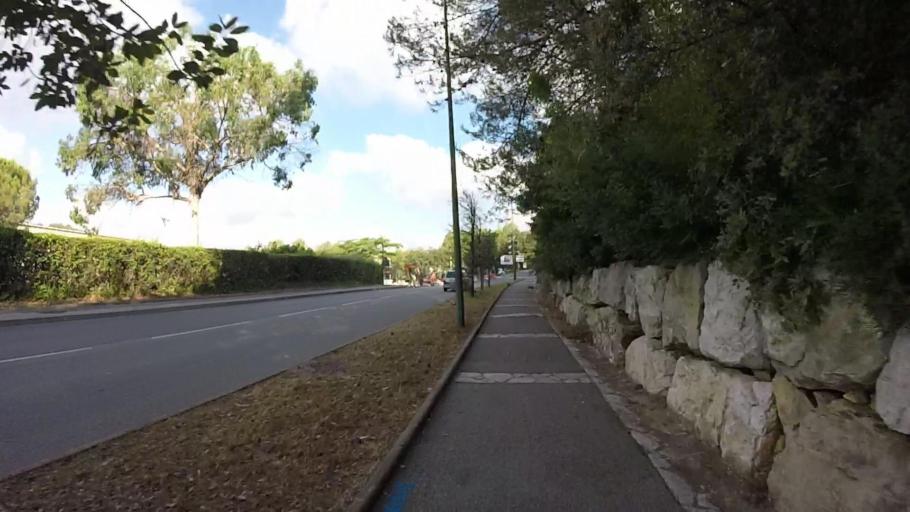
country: FR
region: Provence-Alpes-Cote d'Azur
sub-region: Departement des Alpes-Maritimes
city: Biot
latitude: 43.6214
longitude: 7.0593
